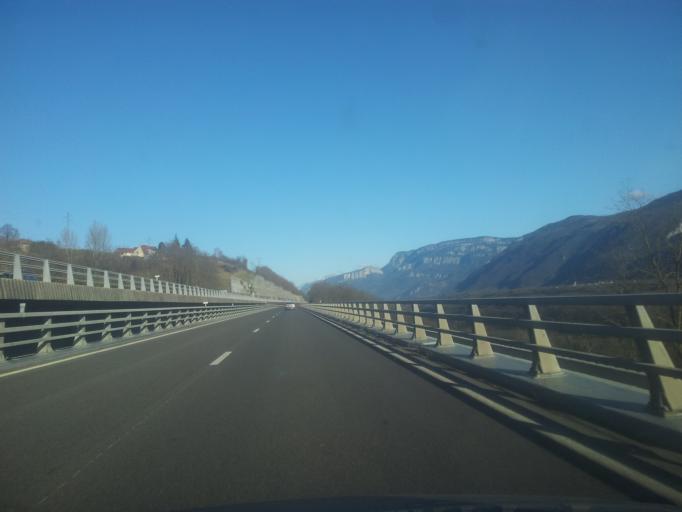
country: FR
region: Rhone-Alpes
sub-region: Departement de l'Isere
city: Saint-Sauveur
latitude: 45.1625
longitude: 5.3663
